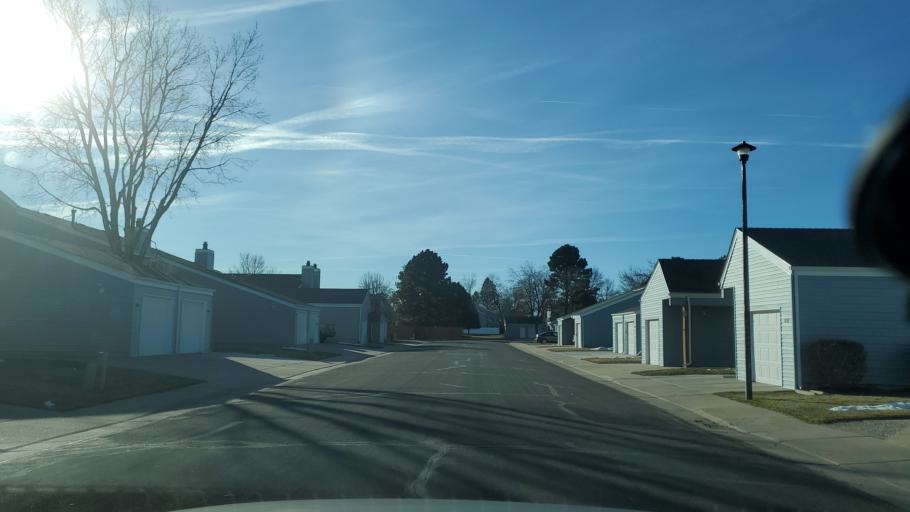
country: US
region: Colorado
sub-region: Adams County
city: Northglenn
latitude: 39.9131
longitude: -104.9445
